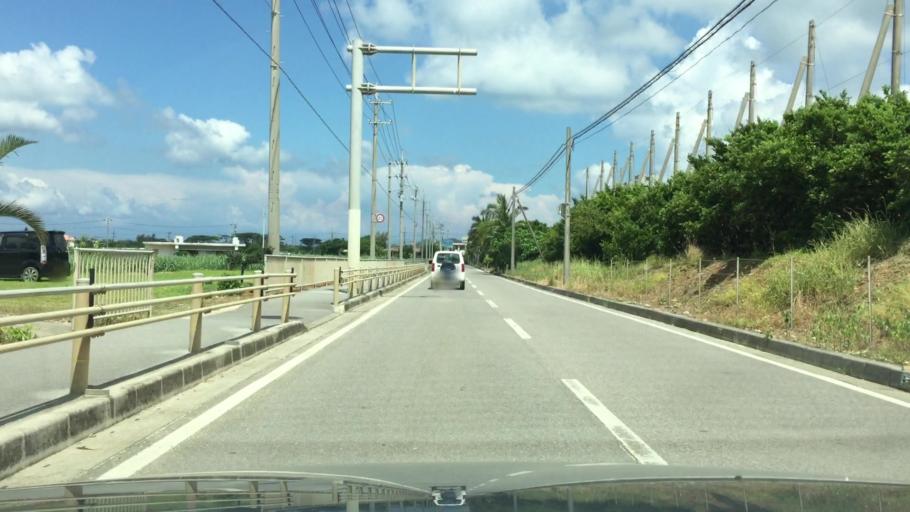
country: JP
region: Okinawa
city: Ishigaki
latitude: 24.3938
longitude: 124.1594
